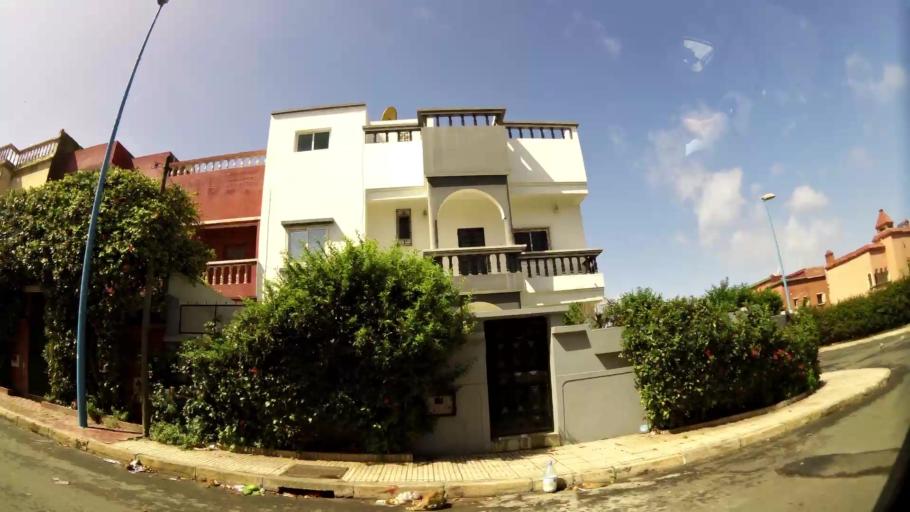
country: MA
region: Grand Casablanca
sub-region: Mediouna
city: Tit Mellil
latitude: 33.6176
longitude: -7.5226
